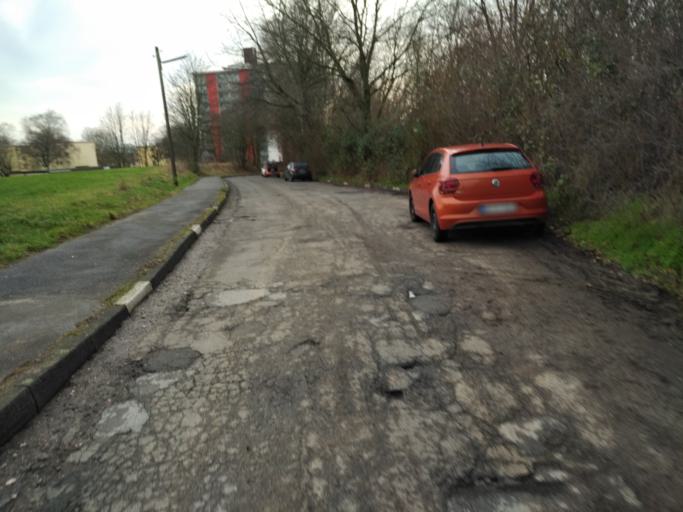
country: DE
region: North Rhine-Westphalia
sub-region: Regierungsbezirk Koln
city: Odenthal
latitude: 51.0516
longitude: 7.0772
